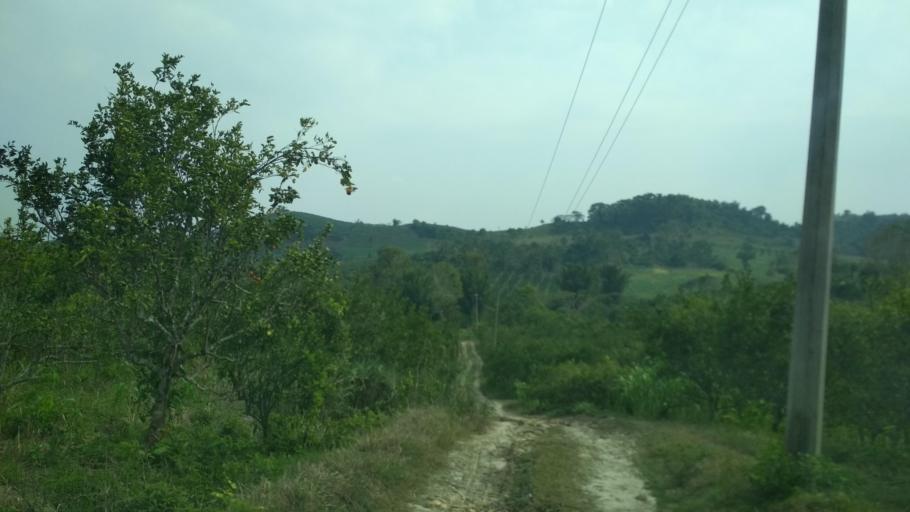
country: MM
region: Kayah
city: Loikaw
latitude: 20.2047
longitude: 97.3200
